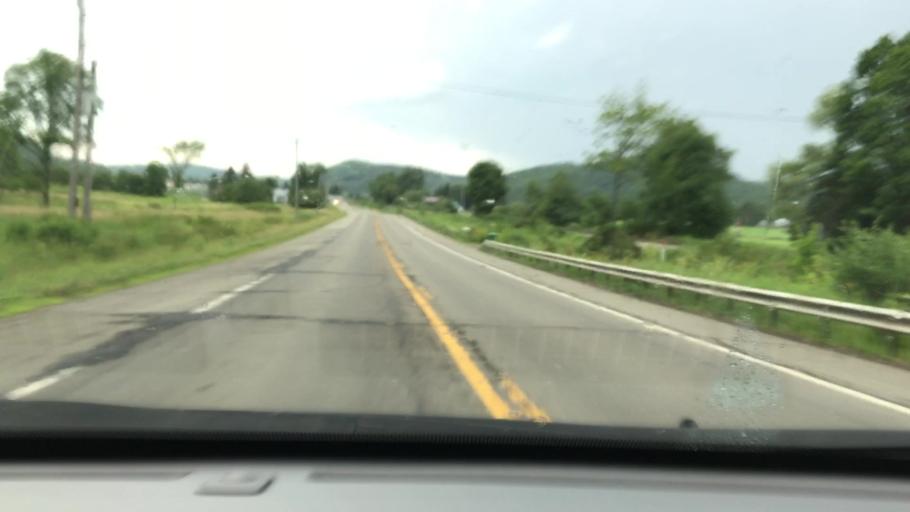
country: US
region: New York
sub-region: Cattaraugus County
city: Salamanca
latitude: 42.2425
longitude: -78.6425
